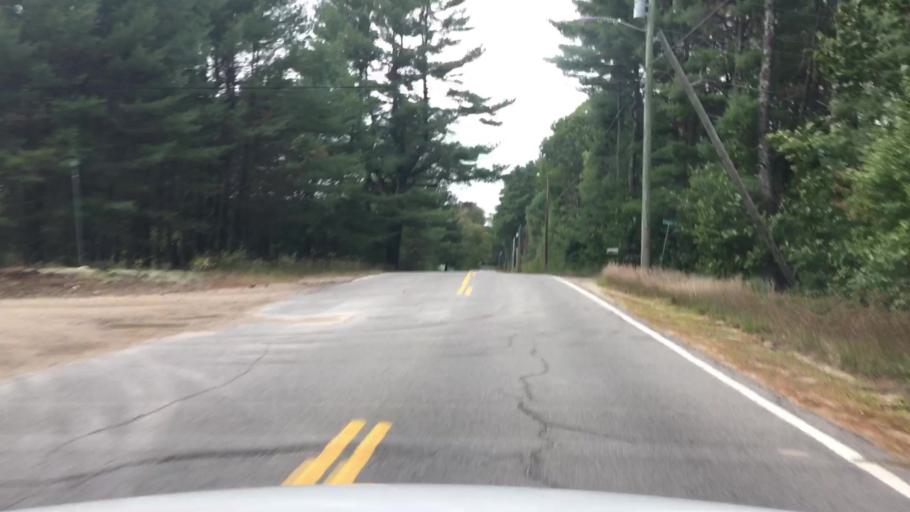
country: US
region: New Hampshire
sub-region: Carroll County
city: Effingham
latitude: 43.7144
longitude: -70.9865
